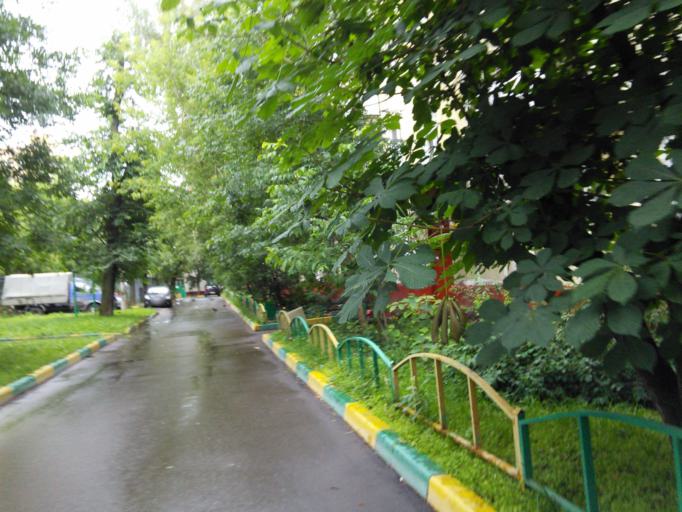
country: RU
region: Moskovskaya
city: Koptevo
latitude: 55.8371
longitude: 37.5323
